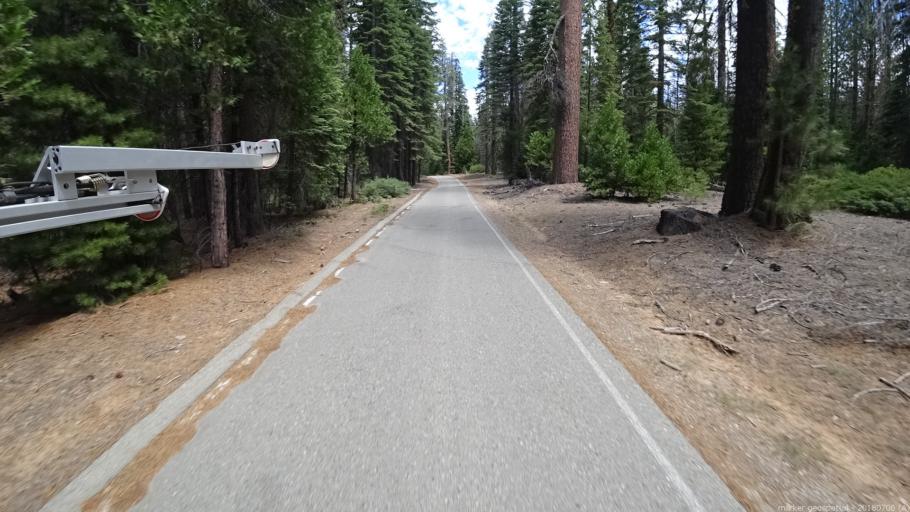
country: US
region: California
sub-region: Madera County
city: Oakhurst
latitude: 37.4173
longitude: -119.4126
